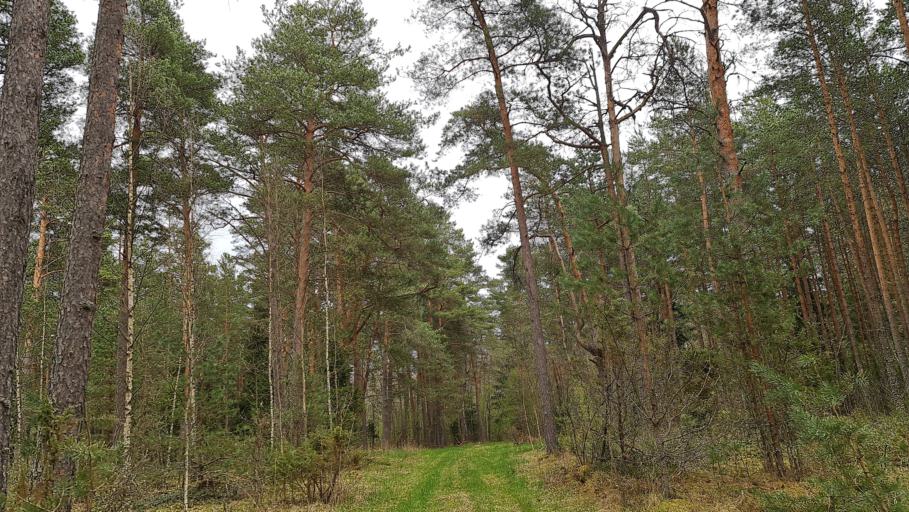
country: BY
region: Vitebsk
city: Byahoml'
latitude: 54.7514
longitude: 28.1475
